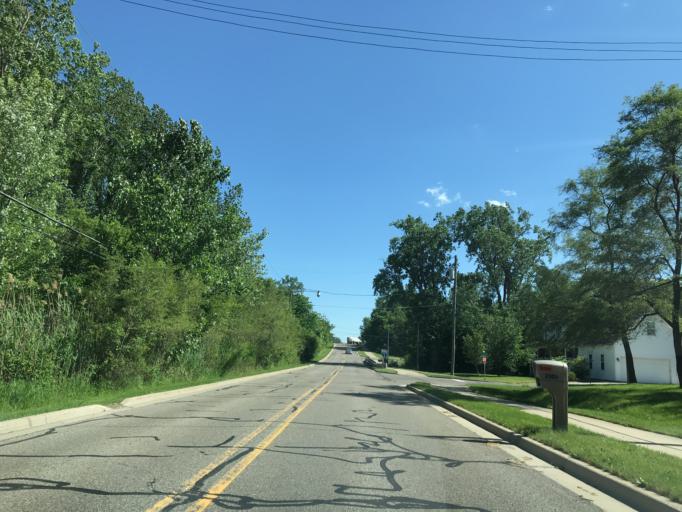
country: US
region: Michigan
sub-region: Oakland County
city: Novi
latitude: 42.5070
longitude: -83.4767
